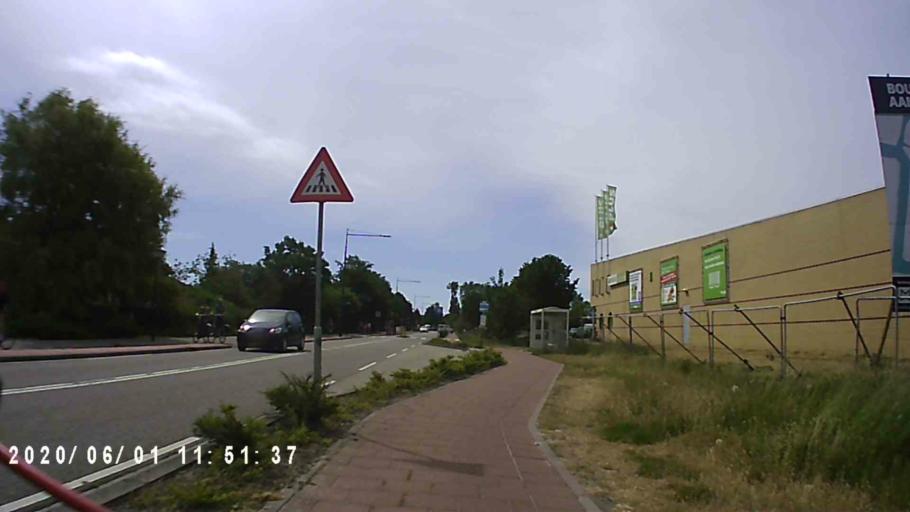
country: NL
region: Friesland
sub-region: Gemeente Harlingen
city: Harlingen
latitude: 53.1658
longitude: 5.4274
